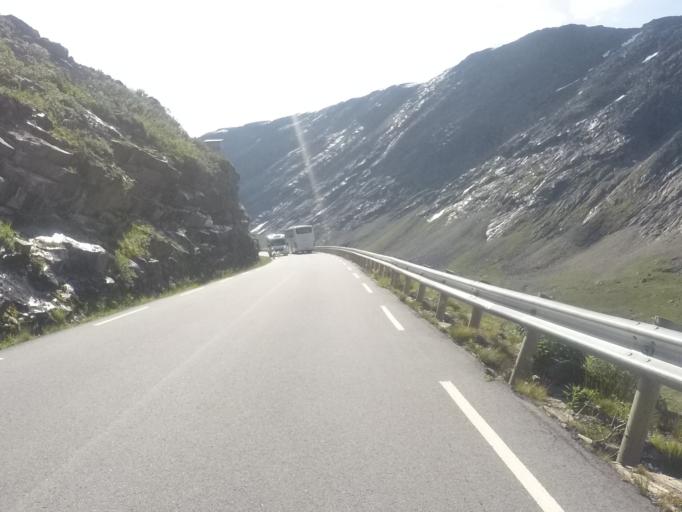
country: NO
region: More og Romsdal
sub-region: Norddal
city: Valldal
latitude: 62.0226
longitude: 7.3430
